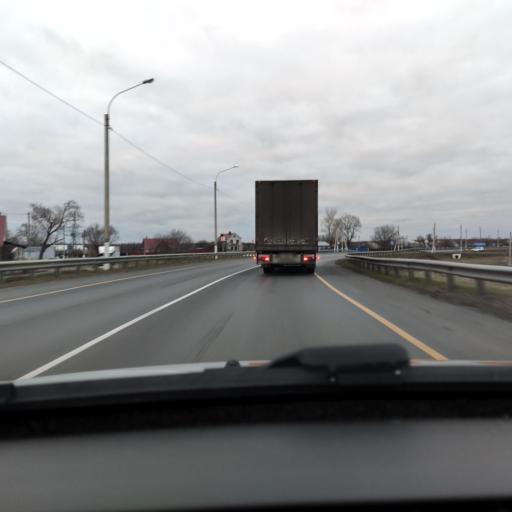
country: RU
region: Lipetsk
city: Khlevnoye
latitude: 52.2589
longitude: 39.1518
